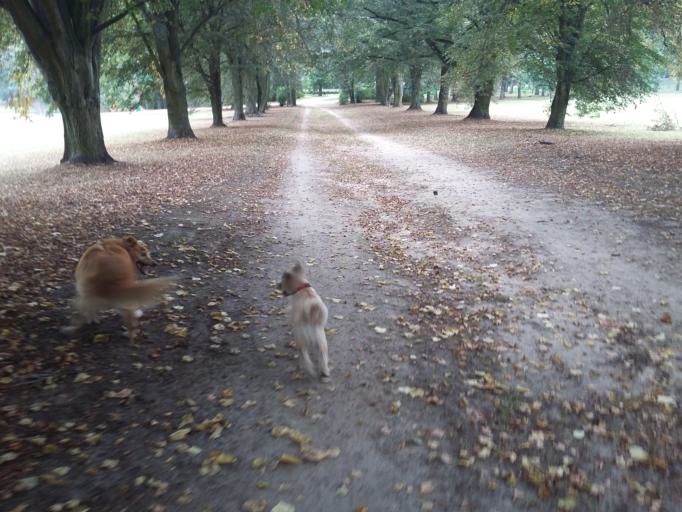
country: PL
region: Lodz Voivodeship
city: Lodz
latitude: 51.7669
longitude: 19.4148
